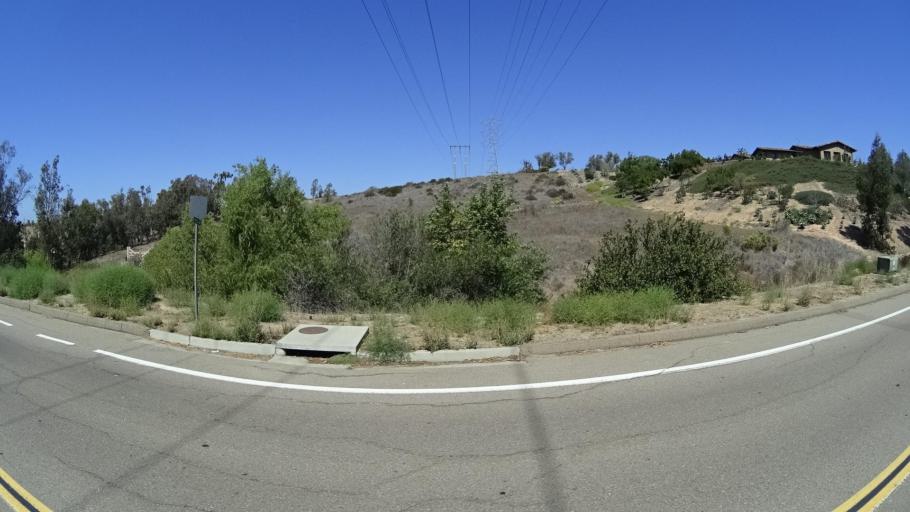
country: US
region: California
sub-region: San Diego County
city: Fairbanks Ranch
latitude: 33.0044
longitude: -117.1693
